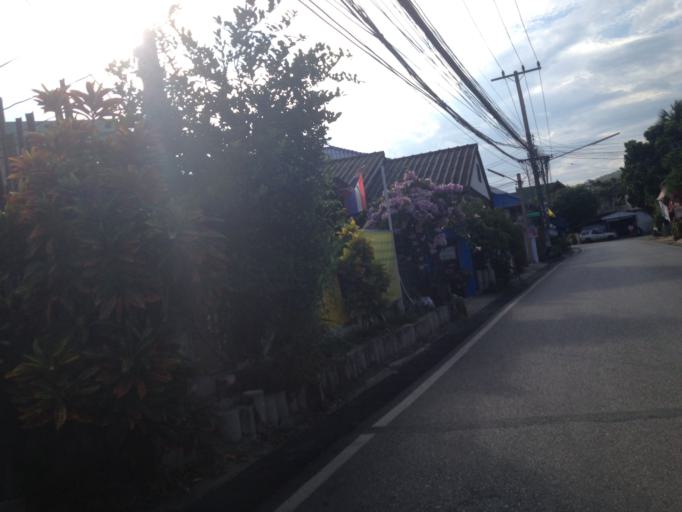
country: TH
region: Chiang Mai
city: Chiang Mai
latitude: 18.7695
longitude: 98.9467
